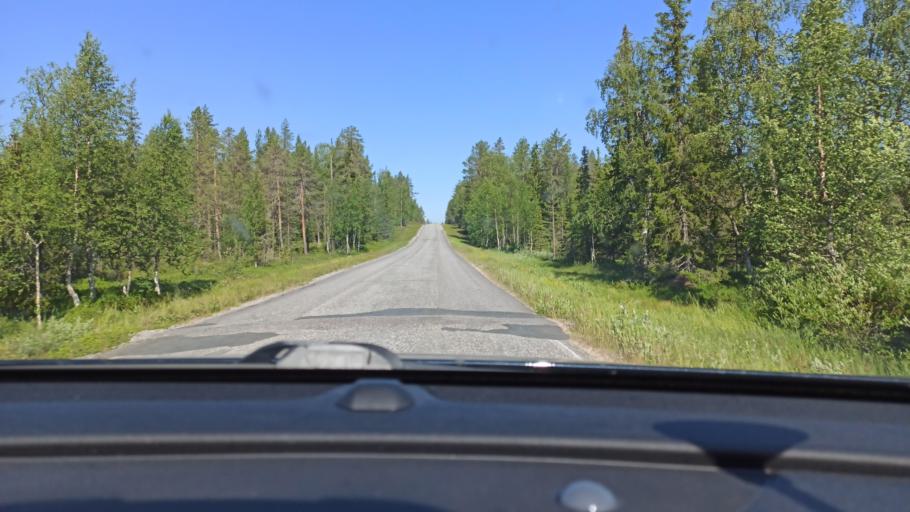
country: FI
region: Lapland
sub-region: Tunturi-Lappi
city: Kolari
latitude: 67.6779
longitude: 24.1415
